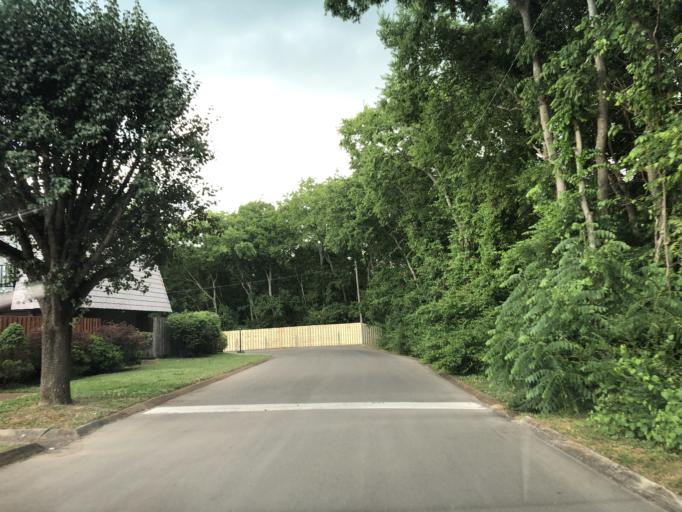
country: US
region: Tennessee
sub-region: Davidson County
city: Goodlettsville
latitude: 36.2763
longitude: -86.6997
